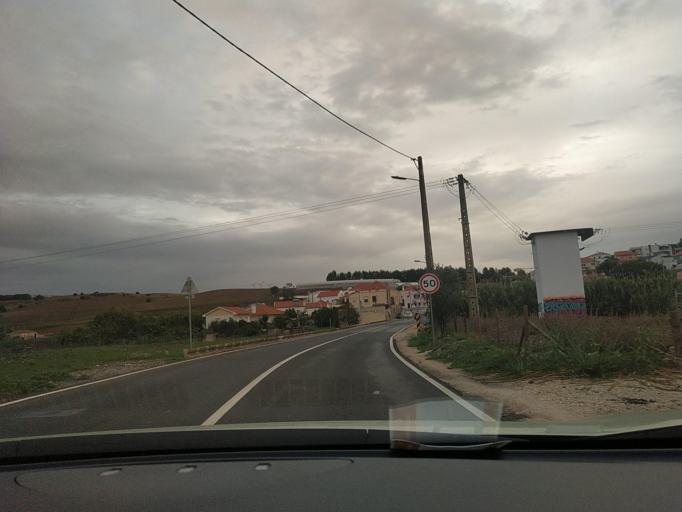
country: PT
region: Lisbon
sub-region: Loures
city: Loures
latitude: 38.8483
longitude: -9.1616
